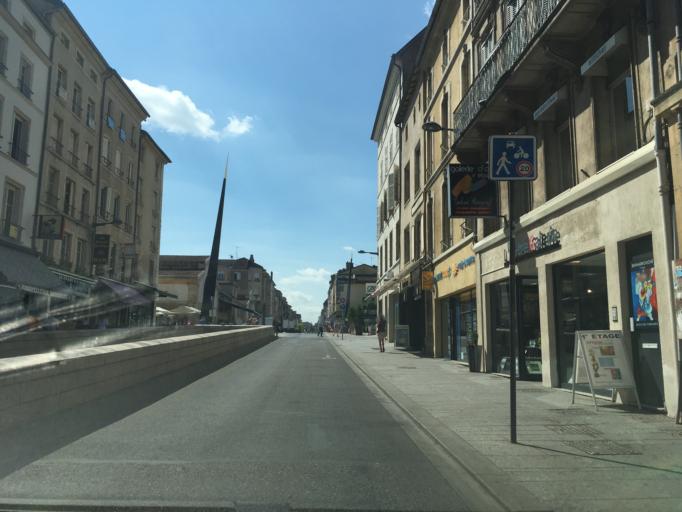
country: FR
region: Lorraine
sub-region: Departement de Meurthe-et-Moselle
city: Nancy
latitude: 48.6900
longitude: 6.1817
